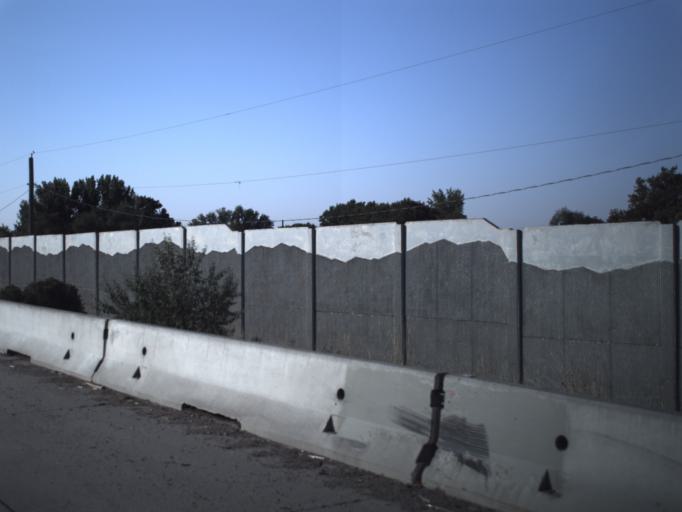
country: US
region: Utah
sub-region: Salt Lake County
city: Salt Lake City
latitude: 40.7907
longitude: -111.9161
